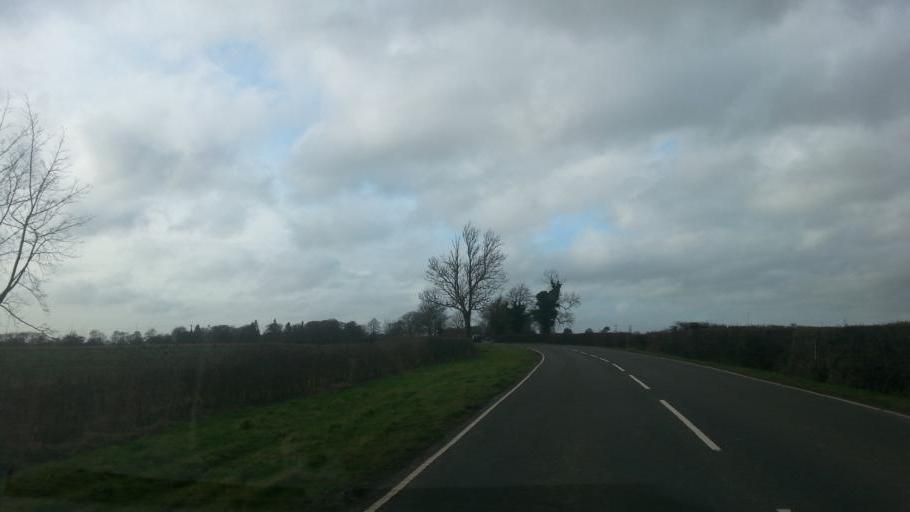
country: GB
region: England
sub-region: District of Rutland
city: Edith Weston
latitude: 52.6359
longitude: -0.6537
